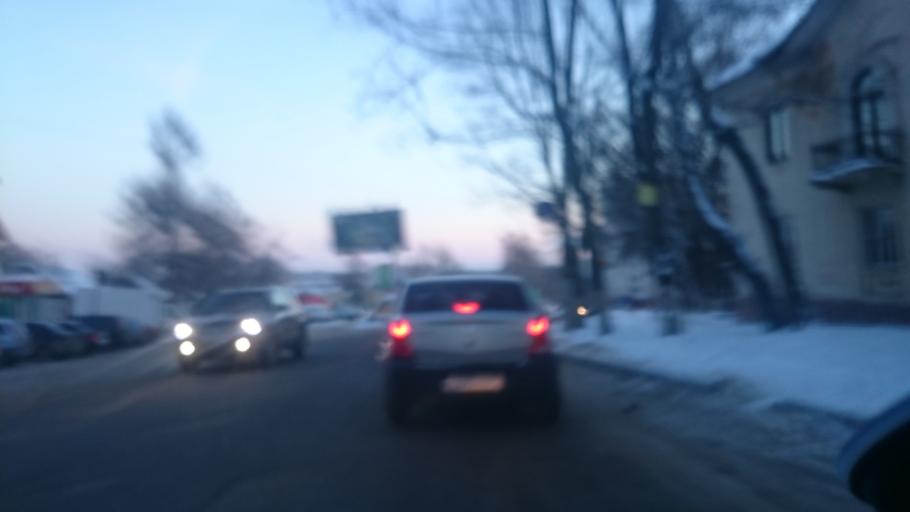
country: RU
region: Tula
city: Mendeleyevskiy
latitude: 54.1632
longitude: 37.5980
